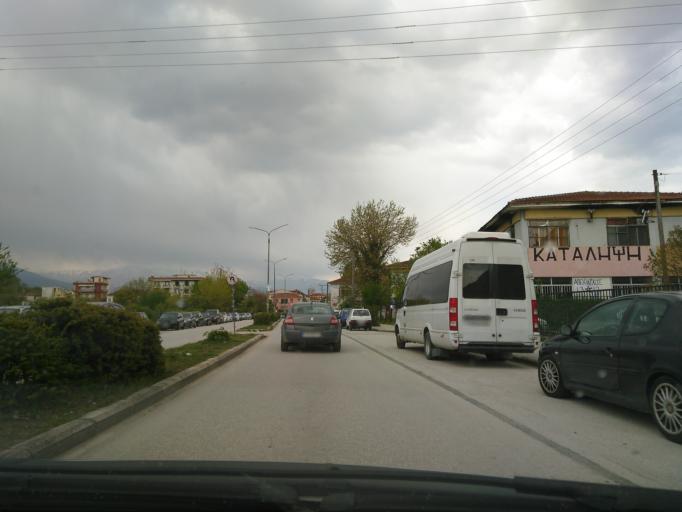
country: GR
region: Epirus
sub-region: Nomos Ioanninon
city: Ioannina
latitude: 39.6718
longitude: 20.8527
